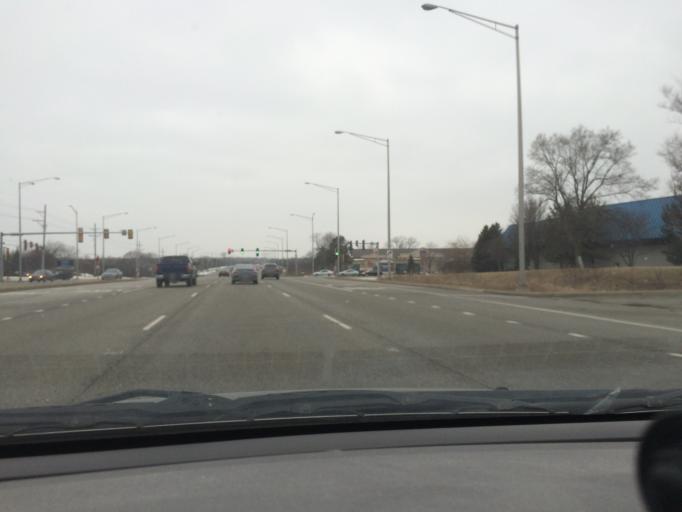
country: US
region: Illinois
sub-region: Cook County
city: Hoffman Estates
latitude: 42.0396
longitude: -88.0487
